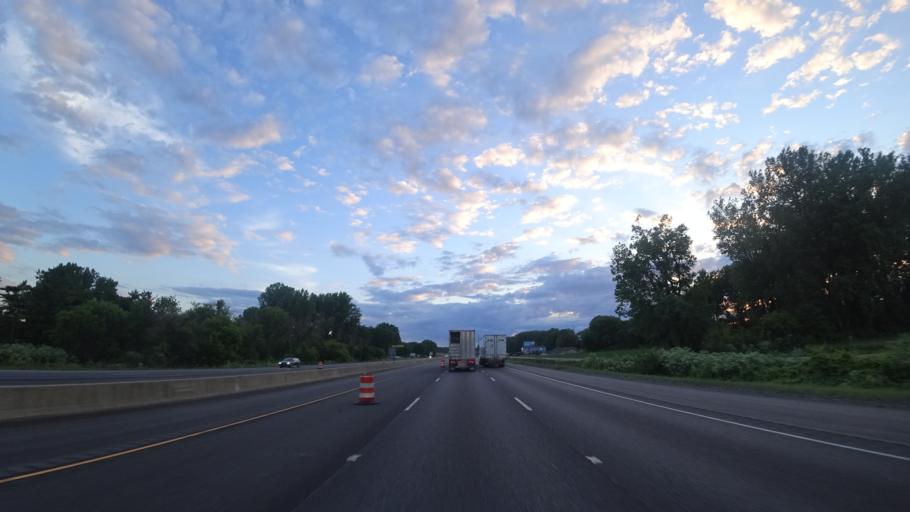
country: US
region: Indiana
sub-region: Porter County
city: Ogden Dunes
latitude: 41.5986
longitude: -87.2024
